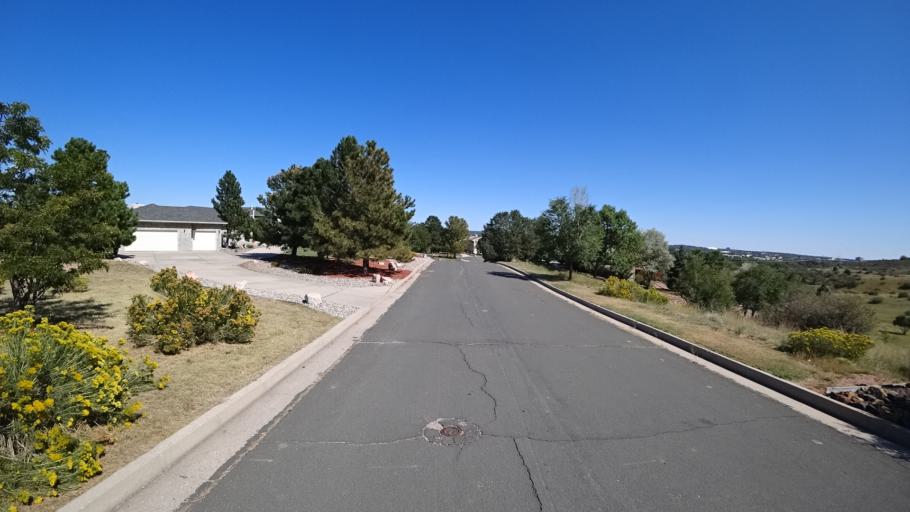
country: US
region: Colorado
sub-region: El Paso County
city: Colorado Springs
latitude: 38.8621
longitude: -104.8438
